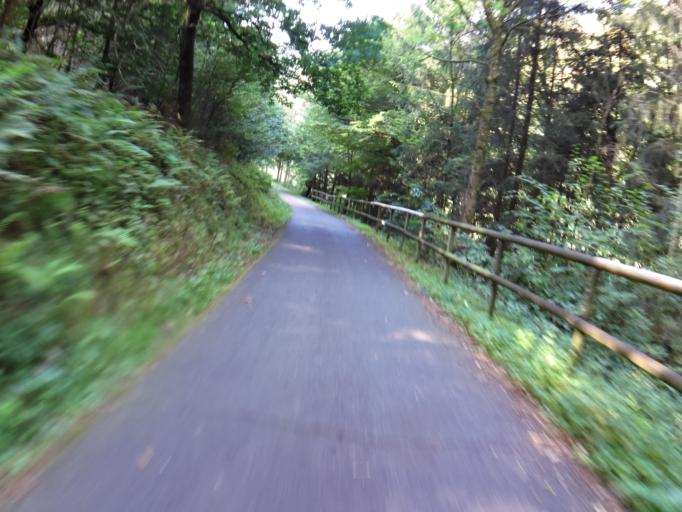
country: DE
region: Rheinland-Pfalz
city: Dahlem
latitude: 49.9211
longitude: 6.6139
